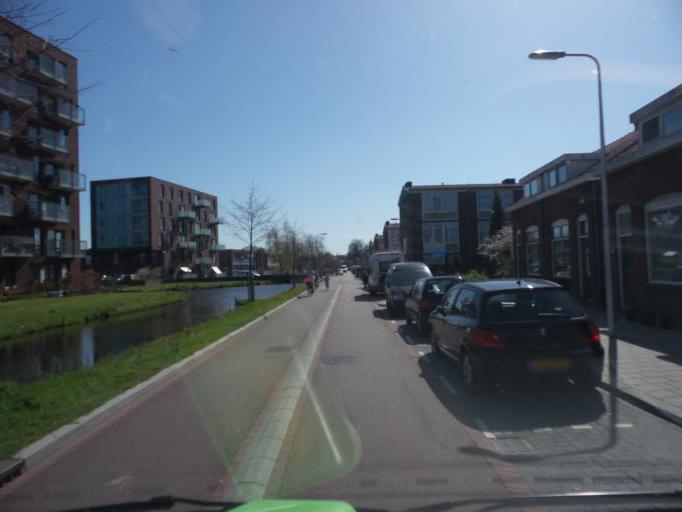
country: NL
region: South Holland
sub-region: Gemeente Gouda
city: Gouda
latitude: 52.0162
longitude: 4.6979
